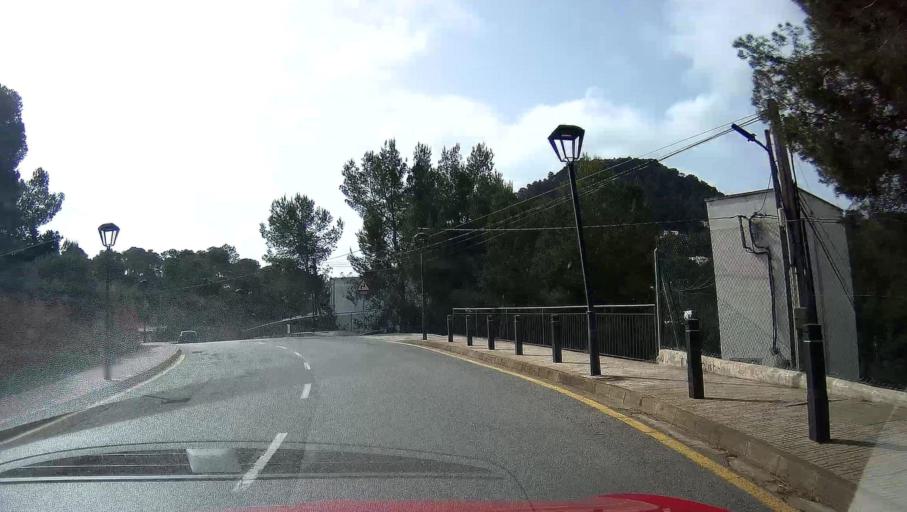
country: ES
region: Balearic Islands
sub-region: Illes Balears
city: Sant Joan de Labritja
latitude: 39.1092
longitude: 1.5189
